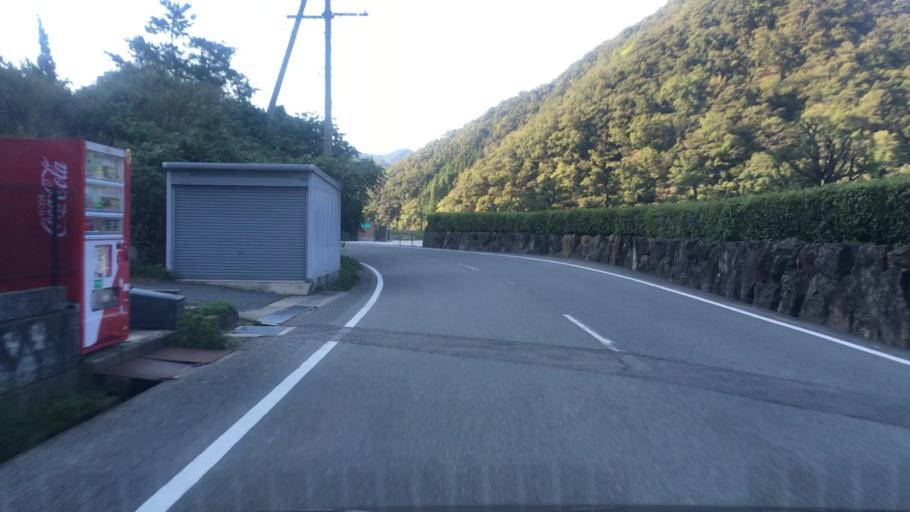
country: JP
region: Hyogo
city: Toyooka
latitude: 35.6155
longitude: 134.8264
